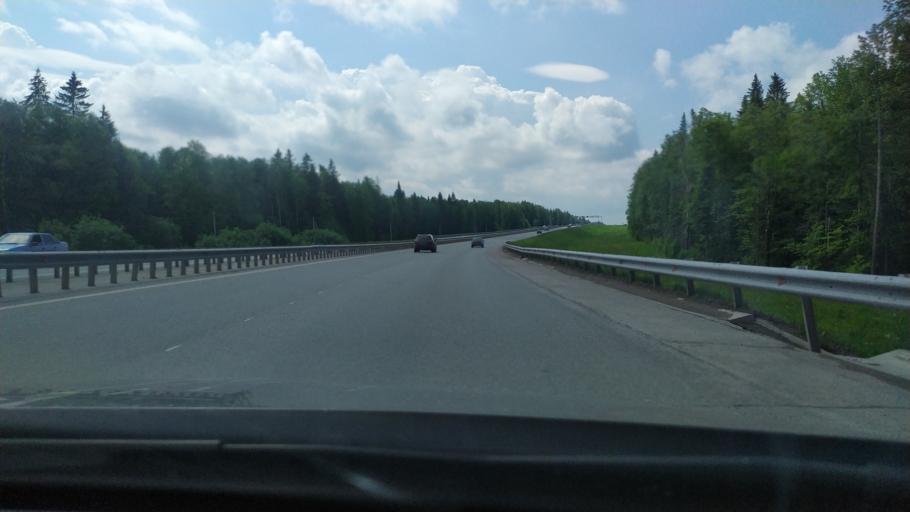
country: RU
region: Perm
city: Novyye Lyady
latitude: 58.0309
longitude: 56.4328
